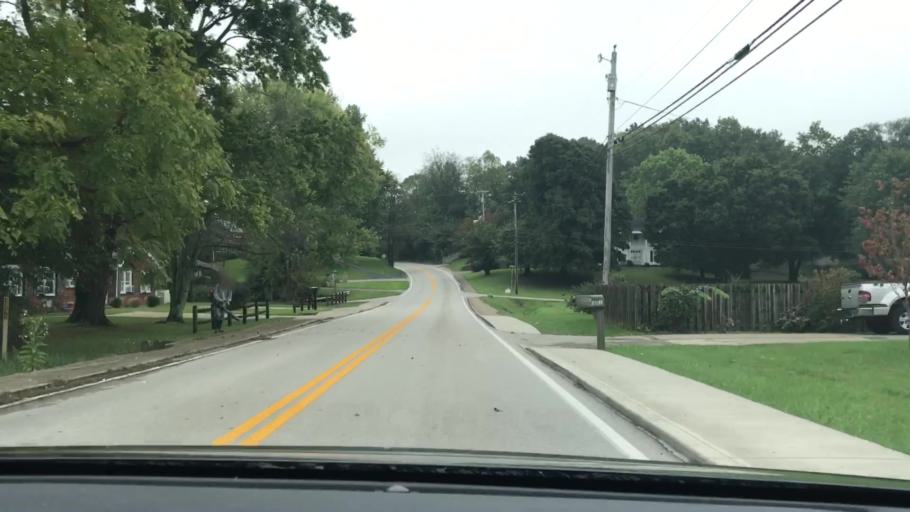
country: US
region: Kentucky
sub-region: Pulaski County
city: Somerset
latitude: 37.0921
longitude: -84.5929
